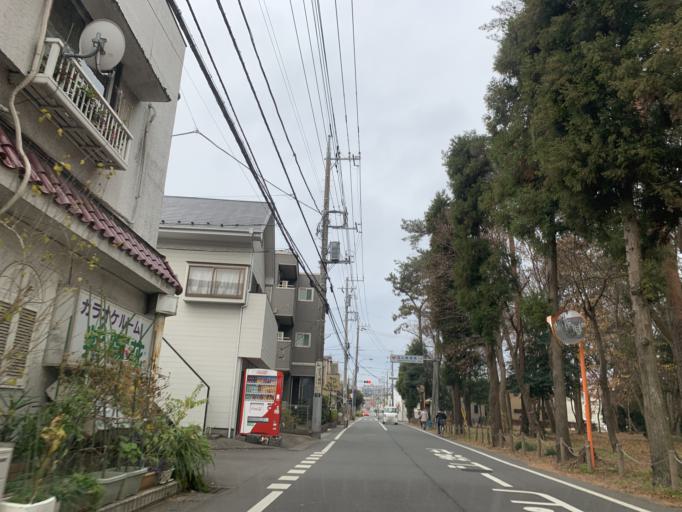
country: JP
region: Chiba
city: Nagareyama
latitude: 35.8805
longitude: 139.9182
